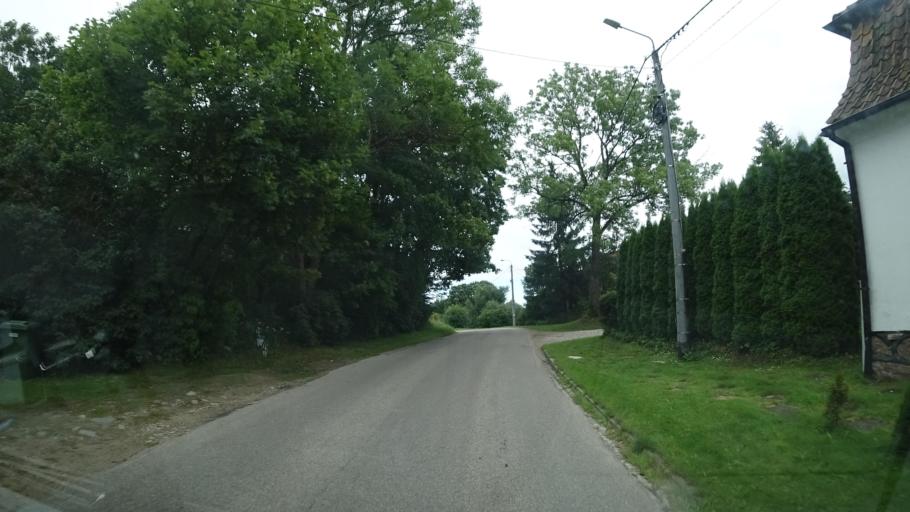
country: PL
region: Podlasie
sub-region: Powiat suwalski
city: Filipow
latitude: 54.2881
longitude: 22.5642
